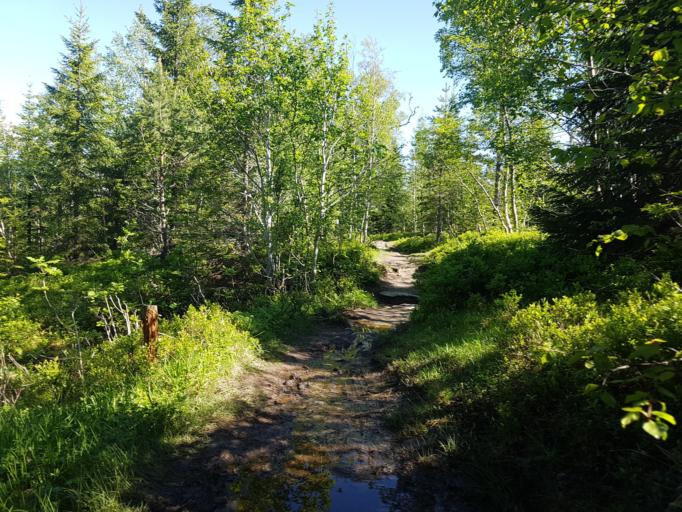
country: NO
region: Sor-Trondelag
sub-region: Trondheim
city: Trondheim
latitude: 63.4214
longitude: 10.2744
